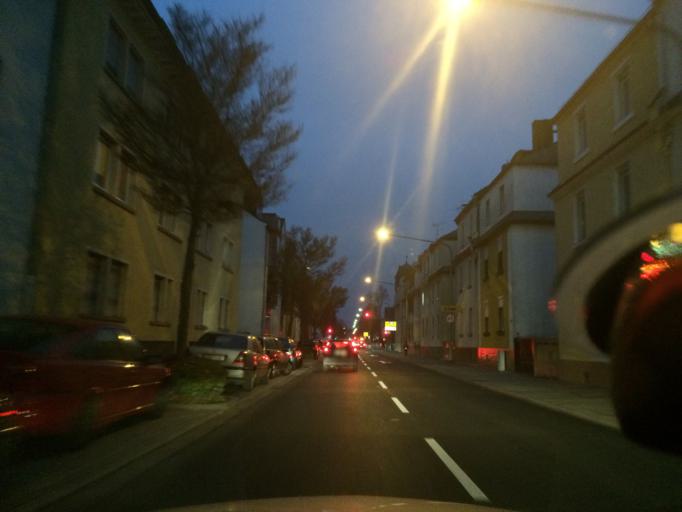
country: DE
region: Hesse
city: Sulzbach
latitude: 50.1111
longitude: 8.5400
